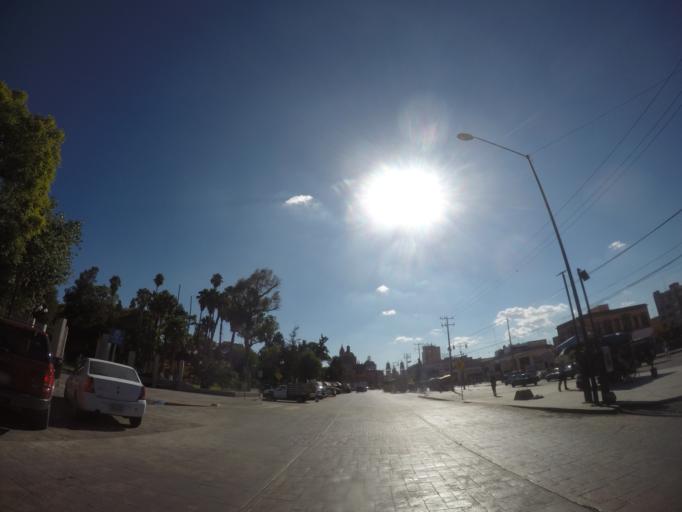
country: MX
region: San Luis Potosi
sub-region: San Luis Potosi
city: San Luis Potosi
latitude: 22.1524
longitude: -100.9712
